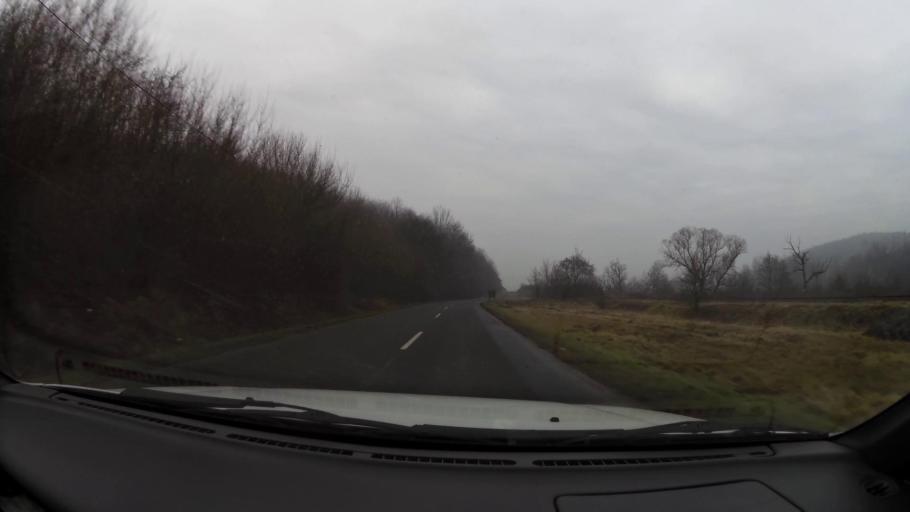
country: HU
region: Borsod-Abauj-Zemplen
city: Rudabanya
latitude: 48.3424
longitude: 20.6443
